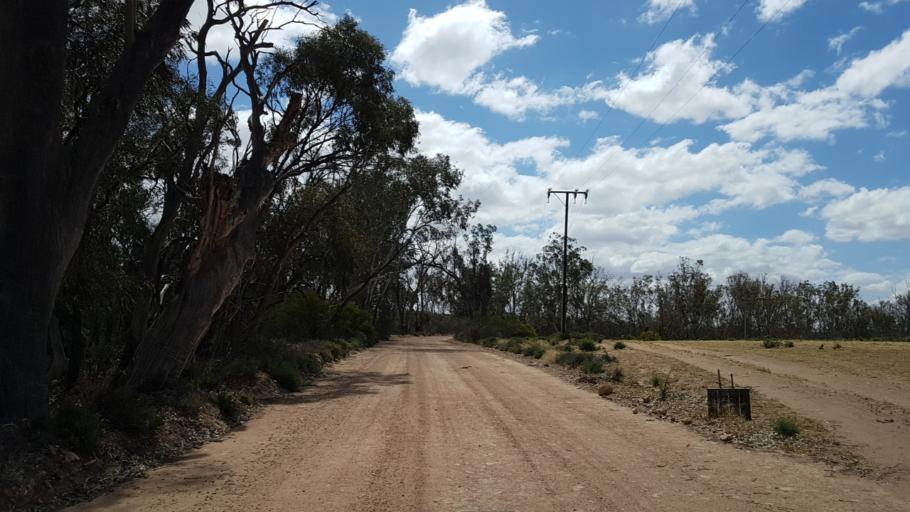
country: AU
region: South Australia
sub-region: Loxton Waikerie
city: Waikerie
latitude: -34.1660
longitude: 140.0249
